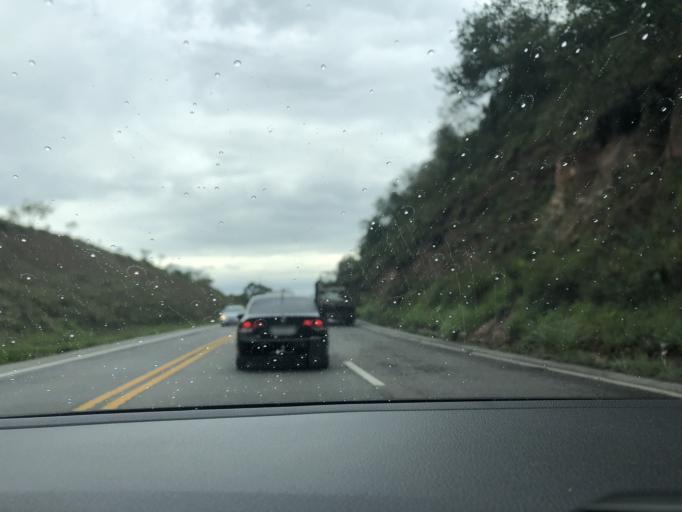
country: BR
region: Sao Paulo
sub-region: Campo Limpo Paulista
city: Campo Limpo Paulista
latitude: -23.1721
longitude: -46.7713
